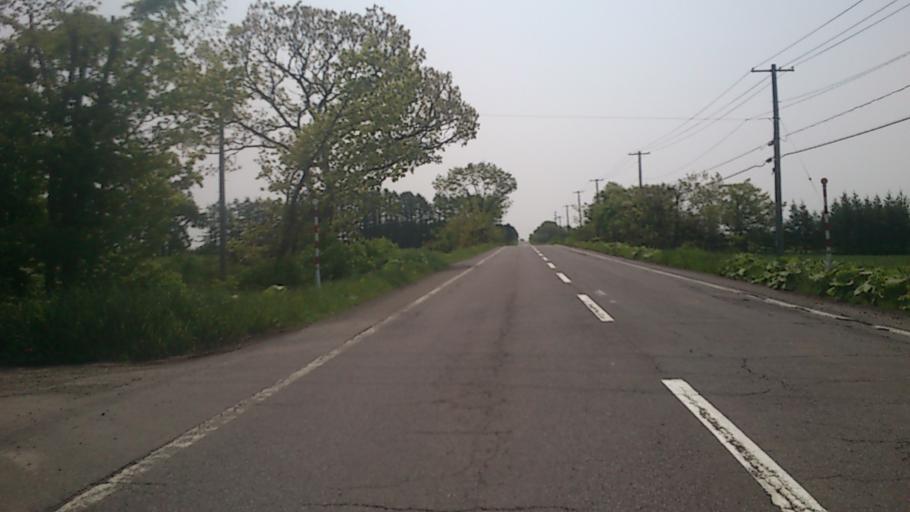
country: JP
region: Hokkaido
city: Shibetsu
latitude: 43.3826
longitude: 144.8352
